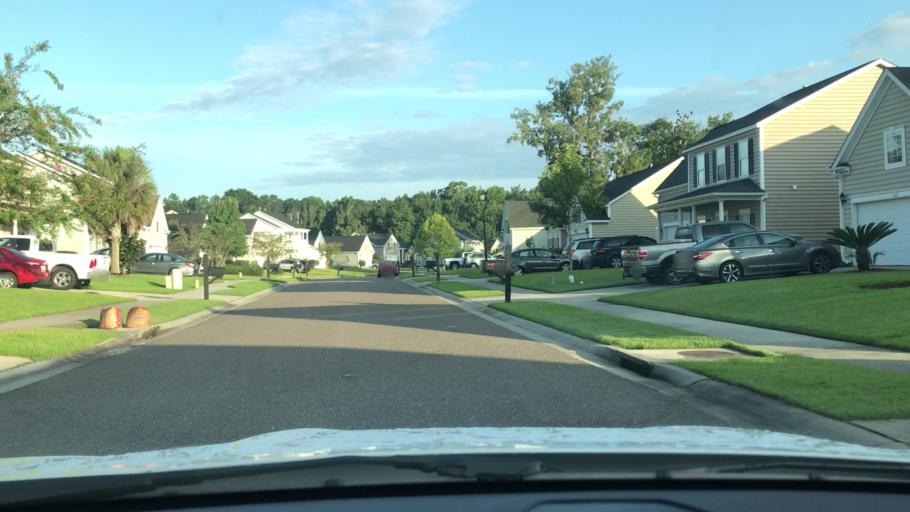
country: US
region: South Carolina
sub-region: Charleston County
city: Shell Point
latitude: 32.8340
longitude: -80.1001
